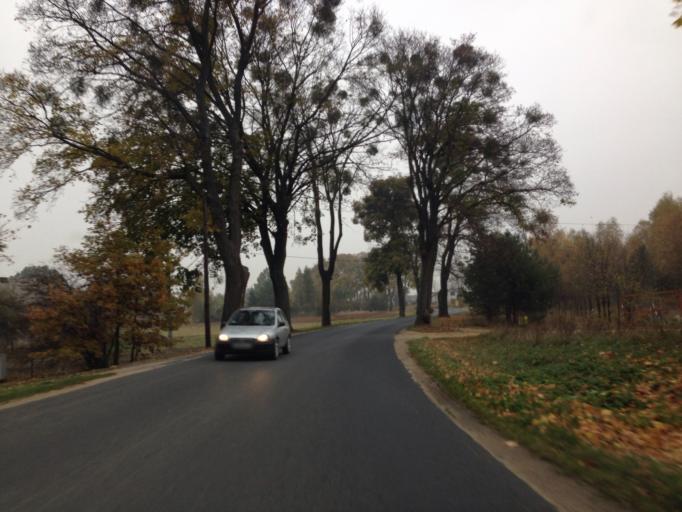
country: PL
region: Kujawsko-Pomorskie
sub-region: Powiat brodnicki
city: Brodnica
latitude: 53.2898
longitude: 19.3901
